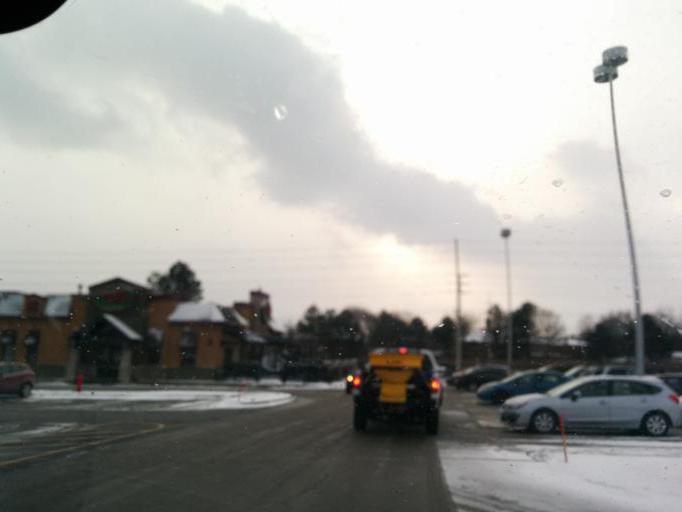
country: CA
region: Ontario
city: Mississauga
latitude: 43.5811
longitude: -79.7595
